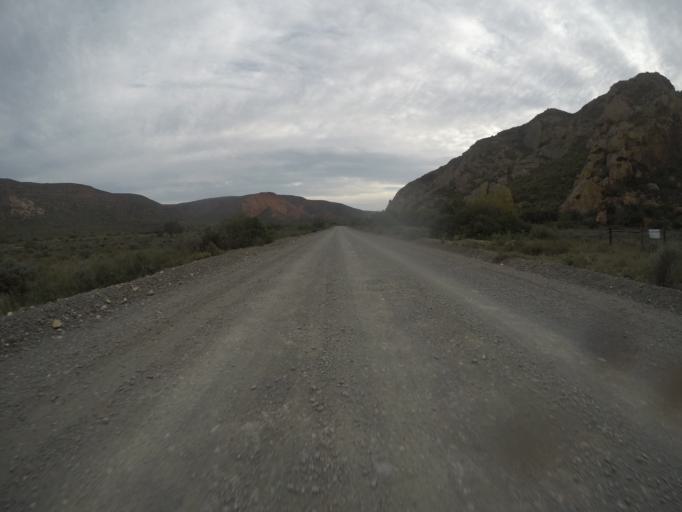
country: ZA
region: Eastern Cape
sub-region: Cacadu District Municipality
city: Willowmore
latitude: -33.5217
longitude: 23.6607
